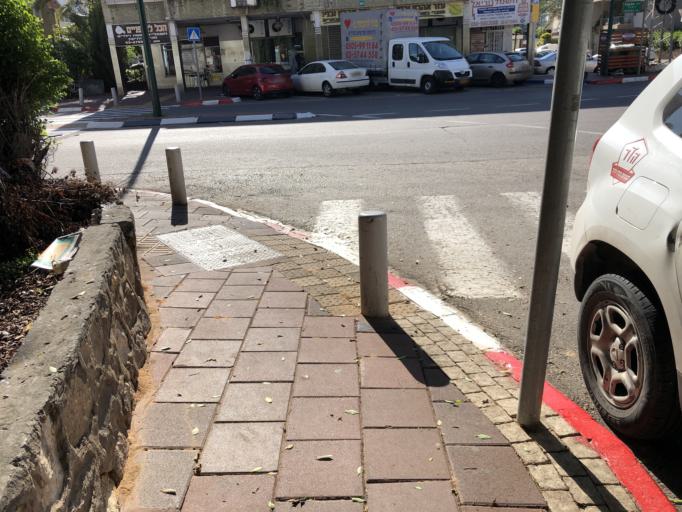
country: IL
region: Tel Aviv
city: Bene Beraq
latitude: 32.0704
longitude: 34.8269
